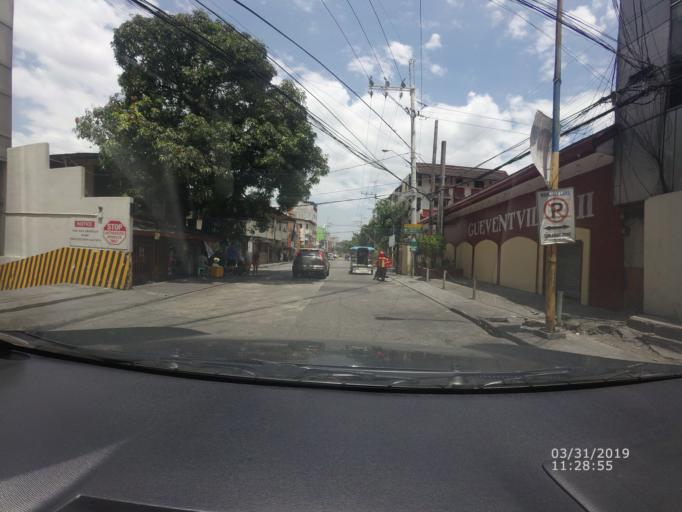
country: PH
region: Metro Manila
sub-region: Mandaluyong
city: Mandaluyong City
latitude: 14.5798
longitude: 121.0456
